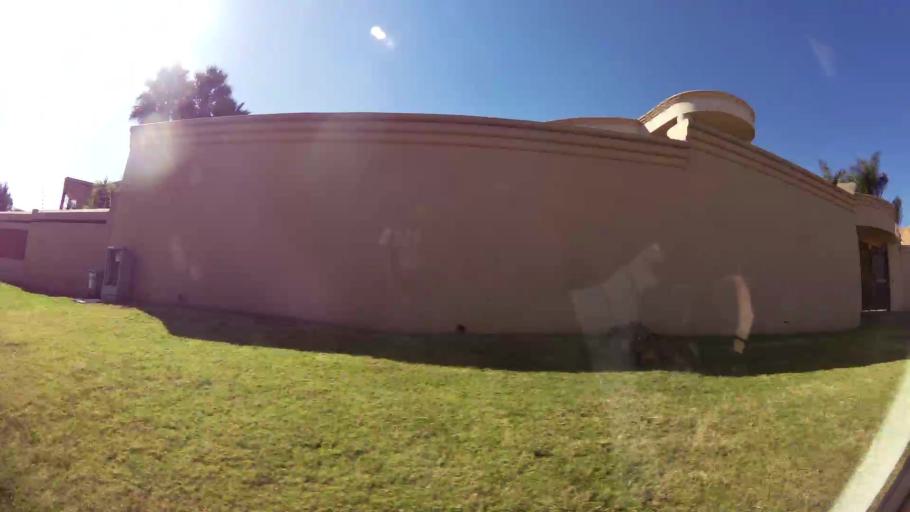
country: ZA
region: Gauteng
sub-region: Ekurhuleni Metropolitan Municipality
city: Germiston
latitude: -26.2930
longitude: 28.0935
